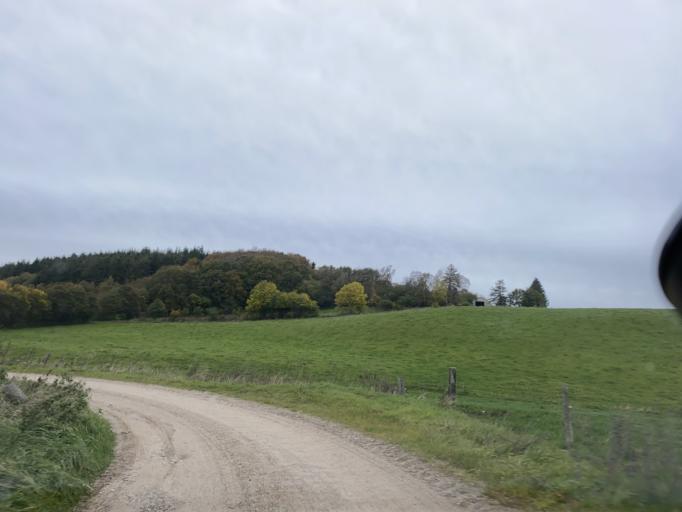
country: DK
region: Central Jutland
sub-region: Favrskov Kommune
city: Hammel
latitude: 56.1963
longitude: 9.7826
